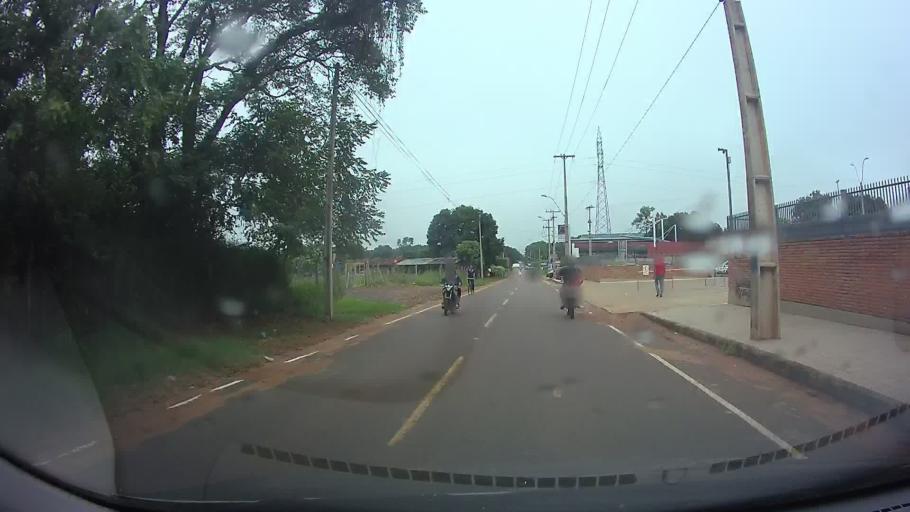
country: PY
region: Central
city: Itaugua
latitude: -25.3807
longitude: -57.3499
